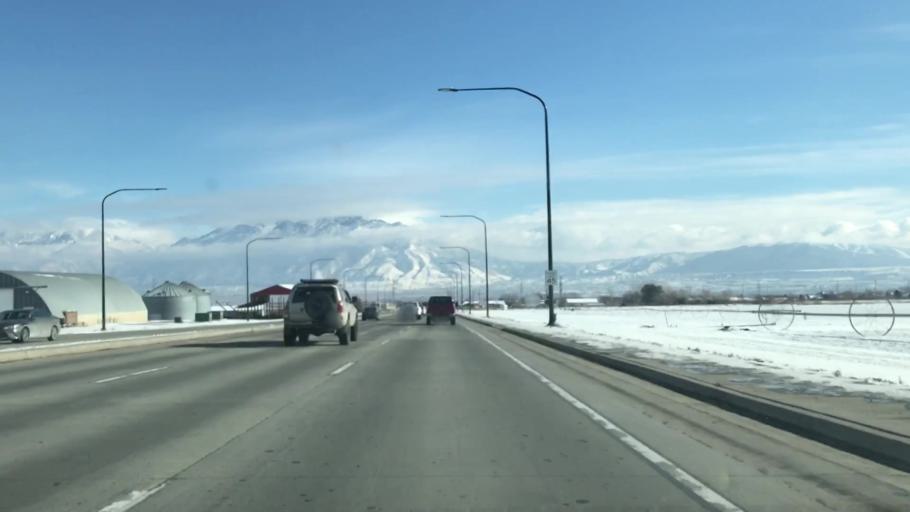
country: US
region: Utah
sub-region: Salt Lake County
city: Herriman
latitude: 40.5078
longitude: -111.9968
